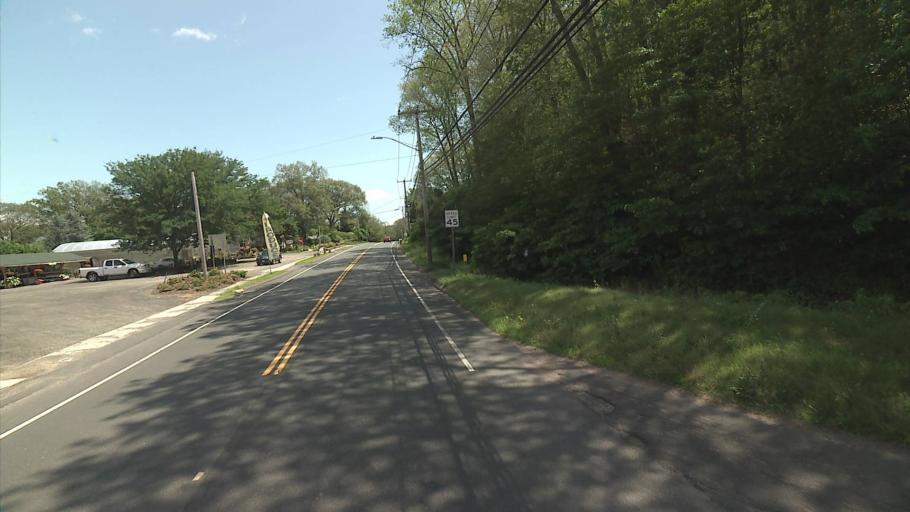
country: US
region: Connecticut
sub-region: Middlesex County
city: East Haddam
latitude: 41.4749
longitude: -72.5062
